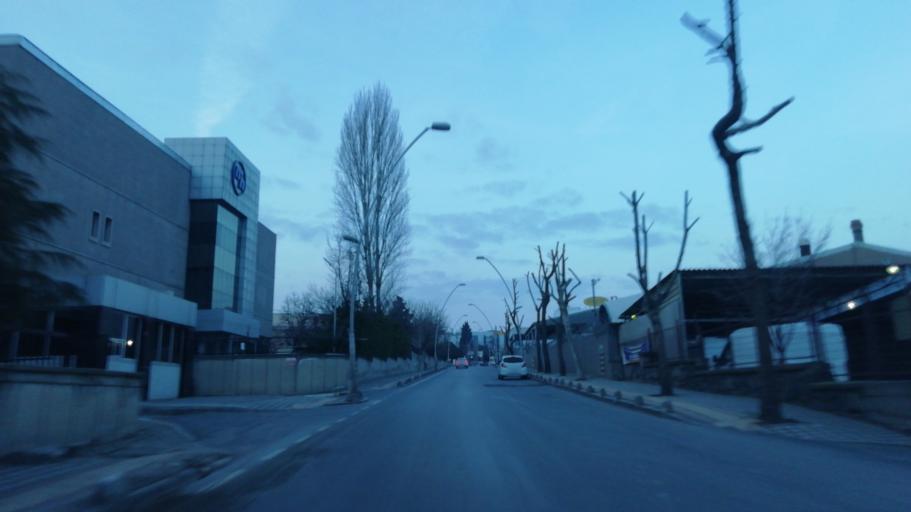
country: TR
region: Istanbul
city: Bahcelievler
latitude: 41.0032
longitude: 28.8217
